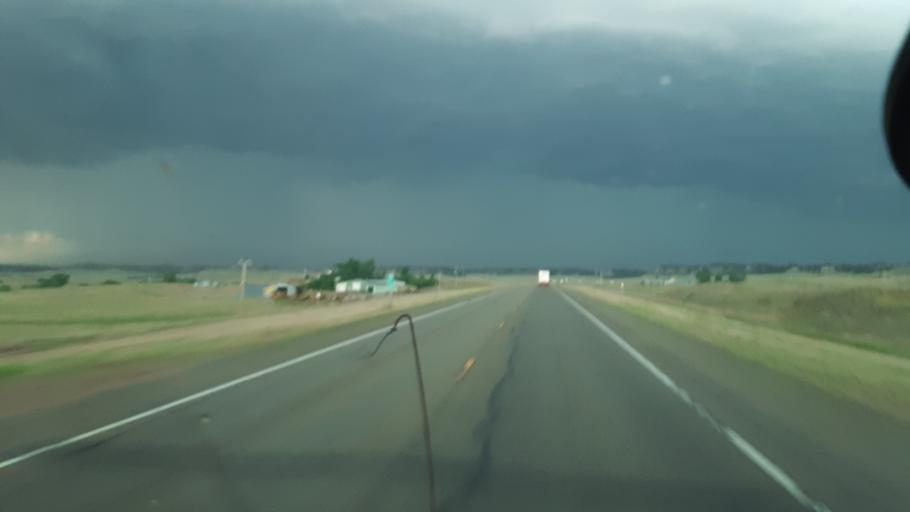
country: US
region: Montana
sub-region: Powder River County
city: Broadus
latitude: 45.4589
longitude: -105.4468
